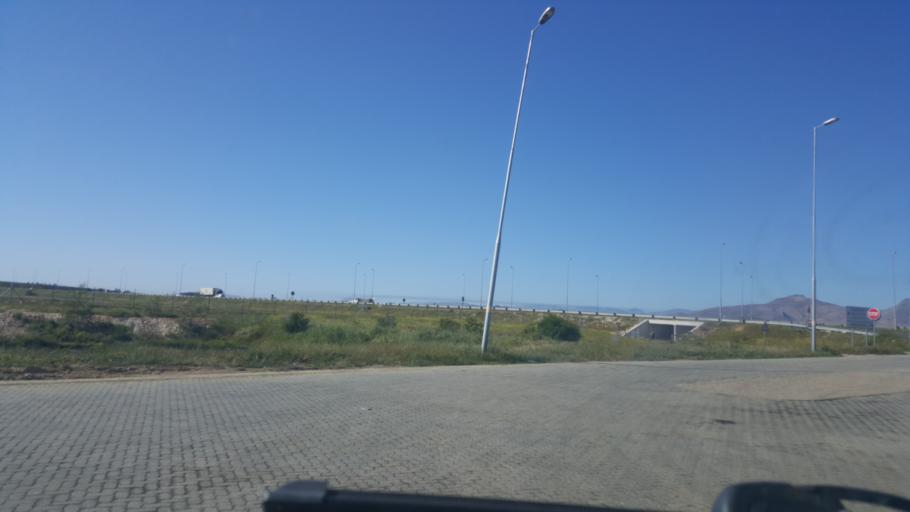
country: ZA
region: Western Cape
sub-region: Cape Winelands District Municipality
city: Worcester
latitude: -33.6334
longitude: 19.3598
